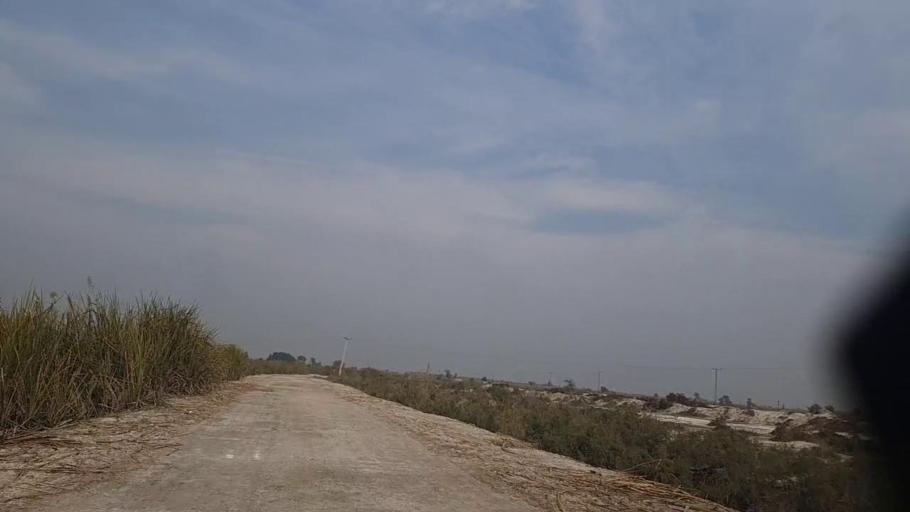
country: PK
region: Sindh
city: Daur
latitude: 26.3693
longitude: 68.2401
